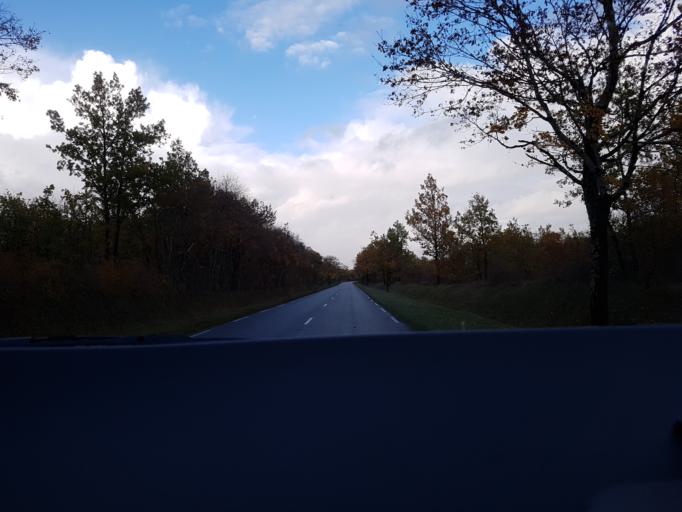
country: FR
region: Poitou-Charentes
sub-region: Departement de la Charente-Maritime
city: Aulnay
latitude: 46.0830
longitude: -0.2975
